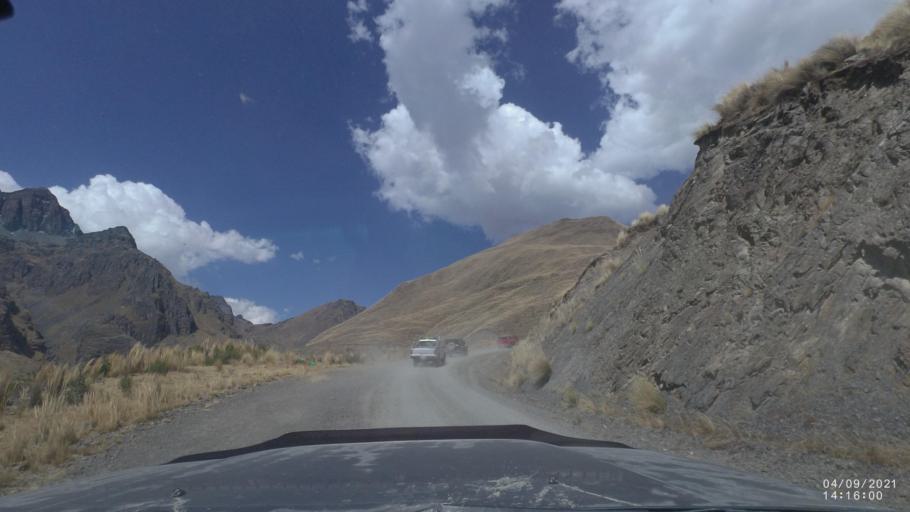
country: BO
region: Cochabamba
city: Sipe Sipe
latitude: -17.2300
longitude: -66.4394
